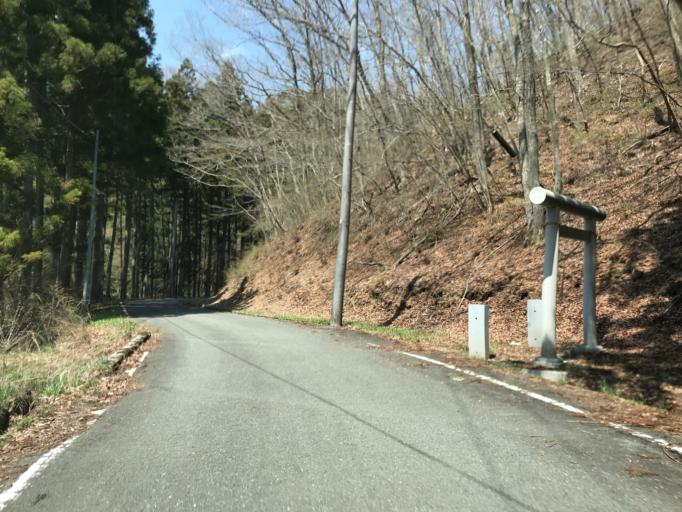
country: JP
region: Fukushima
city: Ishikawa
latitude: 36.9924
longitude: 140.5836
